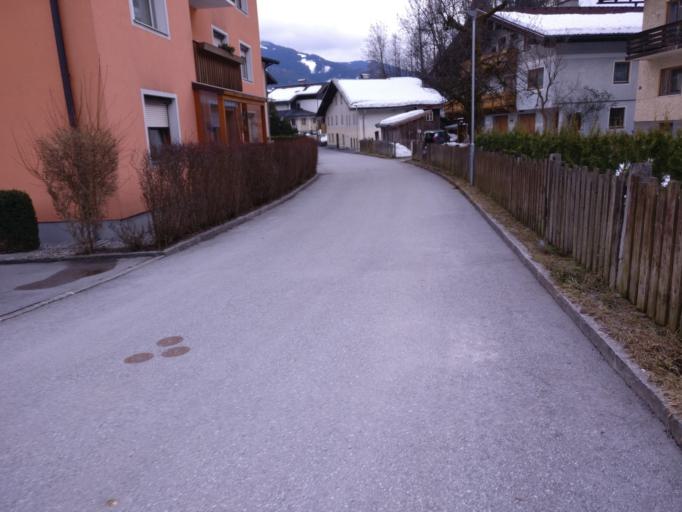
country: AT
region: Salzburg
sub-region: Politischer Bezirk Sankt Johann im Pongau
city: Bischofshofen
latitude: 47.4228
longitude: 13.2137
